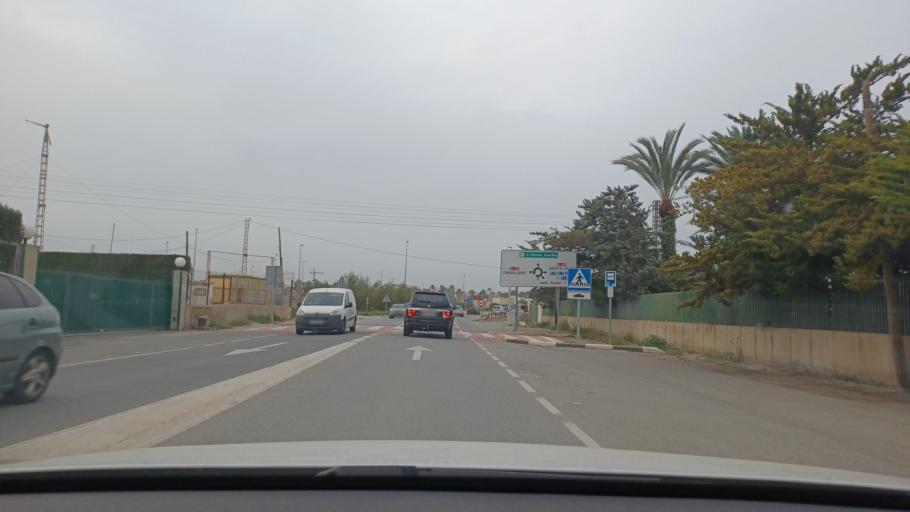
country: ES
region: Valencia
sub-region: Provincia de Alicante
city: Elche
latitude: 38.2508
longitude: -0.6917
